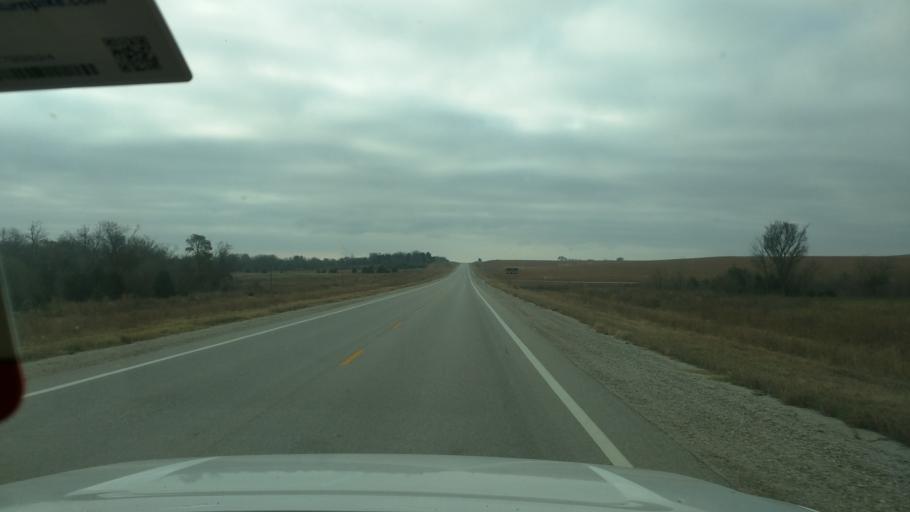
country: US
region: Kansas
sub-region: Elk County
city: Howard
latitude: 37.5937
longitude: -96.2534
